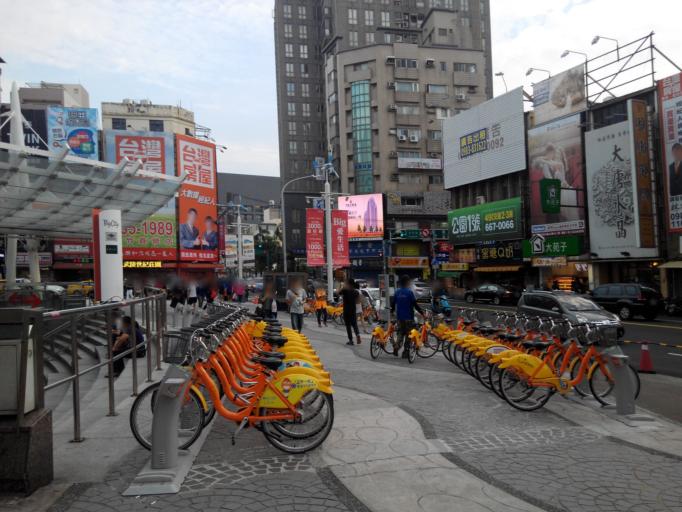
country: TW
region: Taiwan
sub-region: Hsinchu
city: Hsinchu
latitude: 24.8098
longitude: 120.9745
